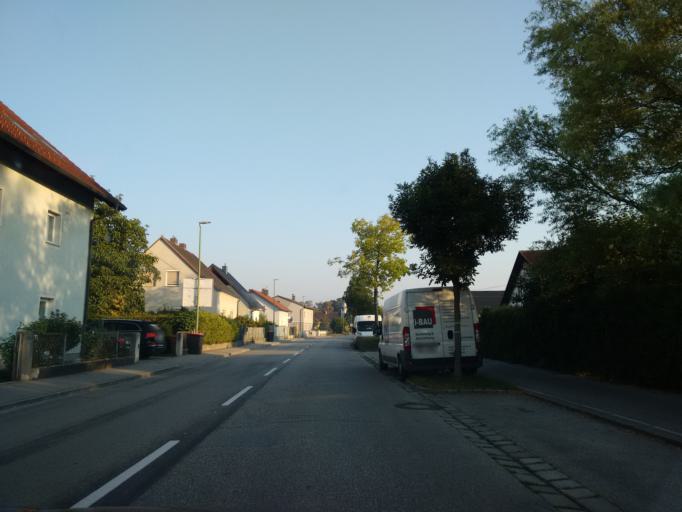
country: AT
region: Upper Austria
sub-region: Wels Stadt
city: Wels
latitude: 48.1737
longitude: 14.0178
